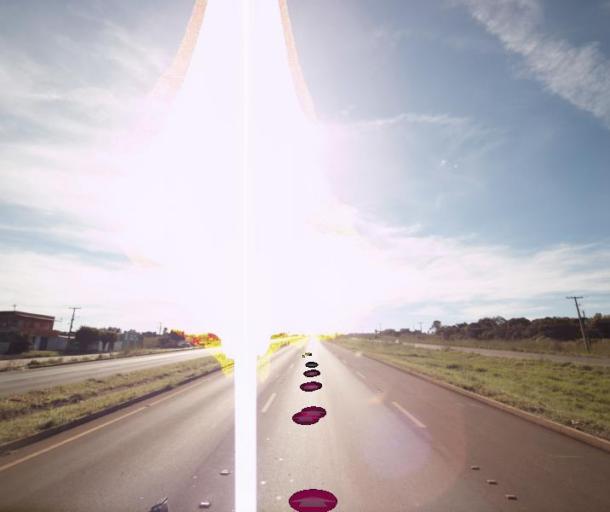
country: BR
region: Federal District
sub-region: Brasilia
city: Brasilia
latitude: -15.7400
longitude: -48.3071
